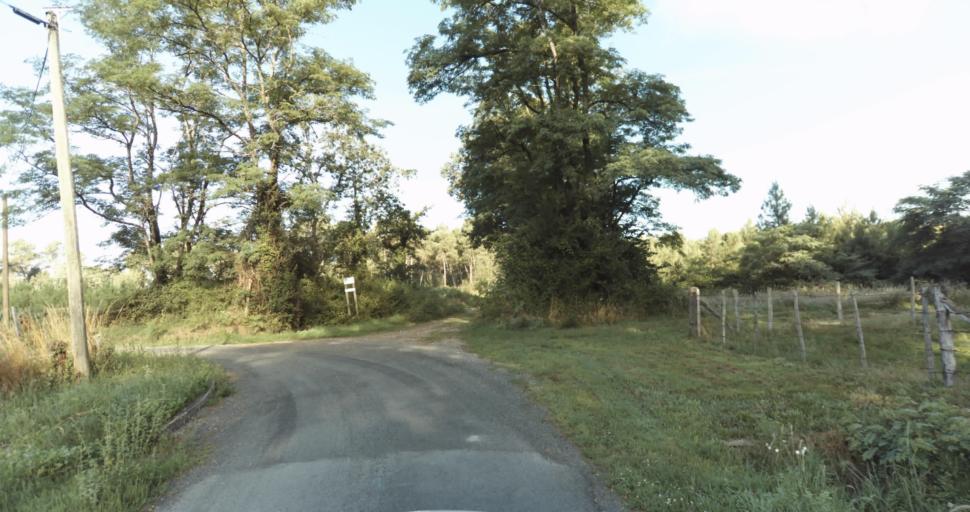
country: FR
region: Aquitaine
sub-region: Departement de la Gironde
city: Bazas
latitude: 44.4466
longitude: -0.2606
